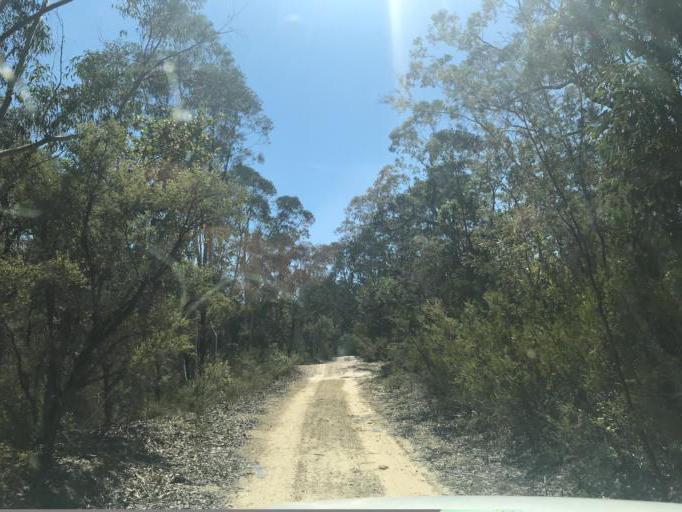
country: AU
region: New South Wales
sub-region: Wyong Shire
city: Little Jilliby
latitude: -33.1508
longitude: 151.1005
